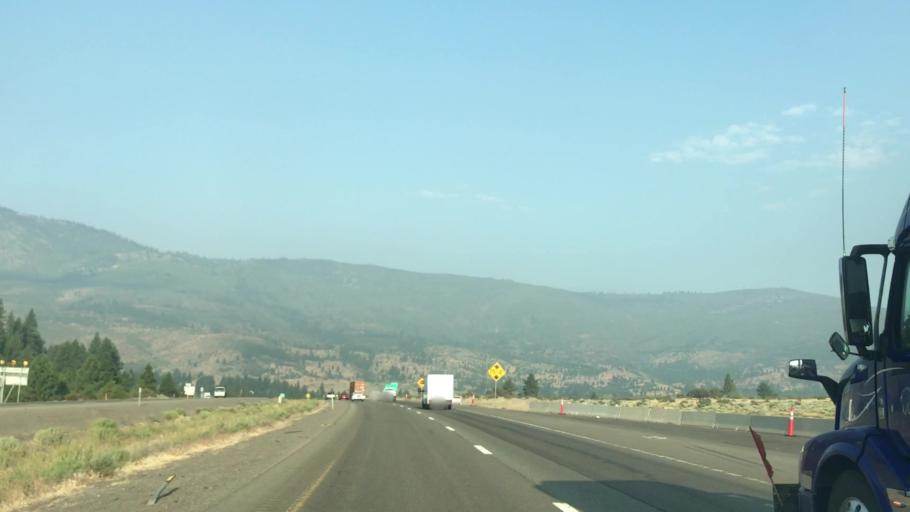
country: US
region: Nevada
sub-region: Washoe County
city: Verdi
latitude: 39.5145
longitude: -119.9830
